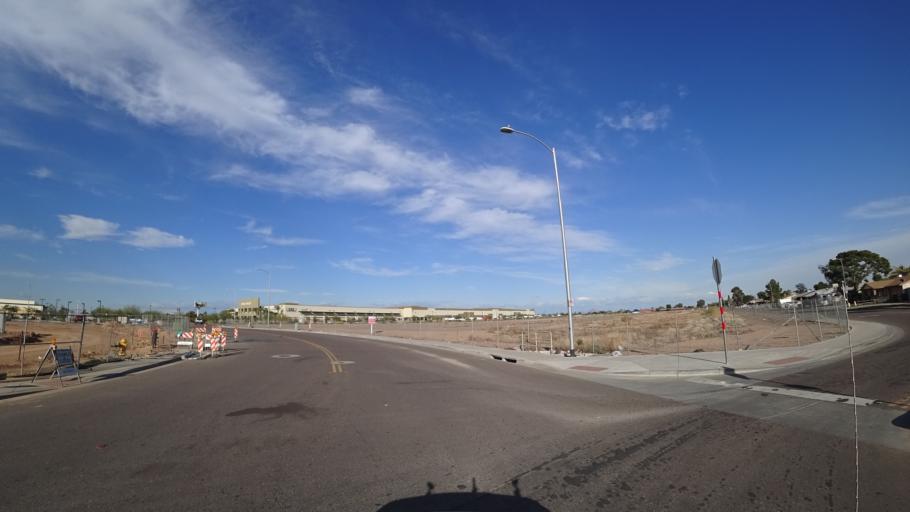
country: US
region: Arizona
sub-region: Maricopa County
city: Tolleson
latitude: 33.4588
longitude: -112.2024
